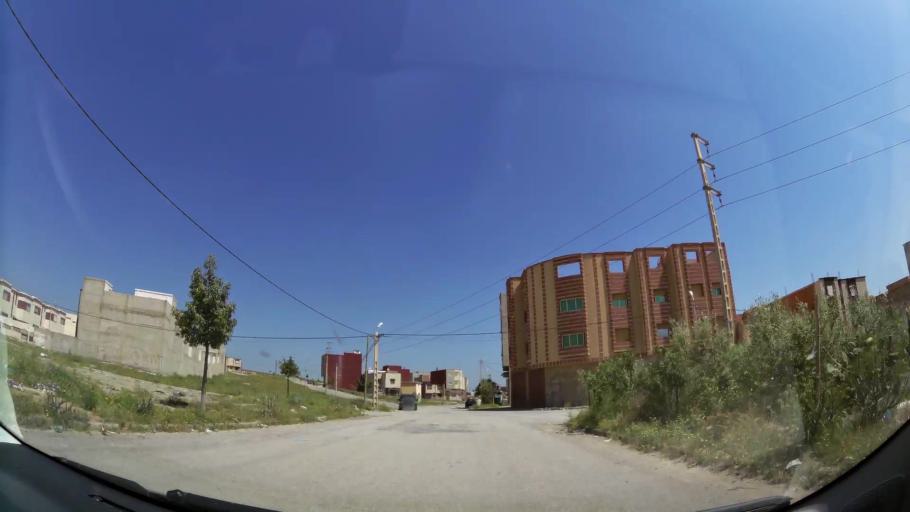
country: MA
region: Oriental
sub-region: Oujda-Angad
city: Oujda
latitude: 34.6747
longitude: -1.9450
